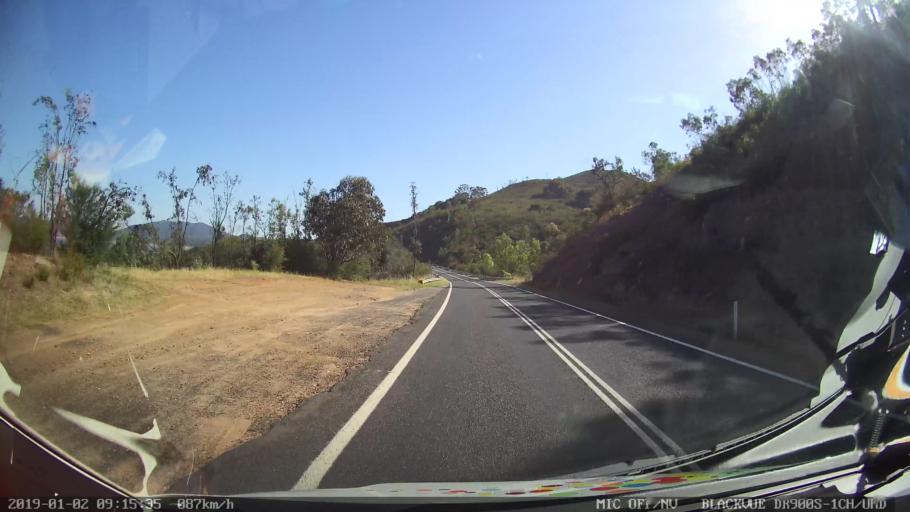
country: AU
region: New South Wales
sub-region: Tumut Shire
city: Tumut
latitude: -35.4634
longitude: 148.2806
